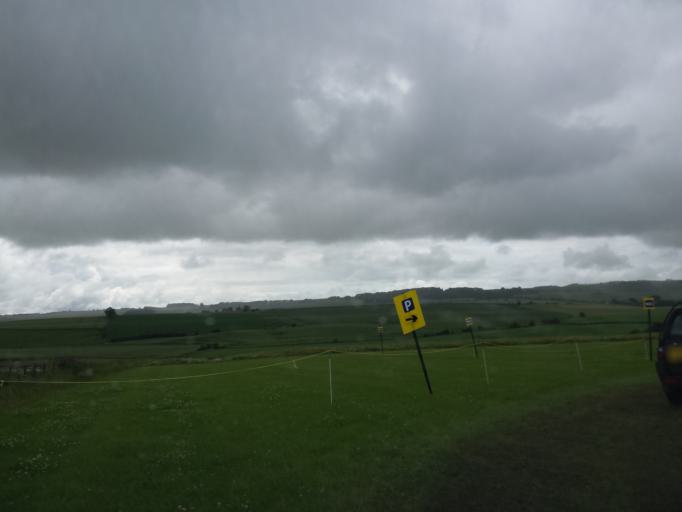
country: GB
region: Scotland
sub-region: Fife
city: Leuchars
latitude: 56.3581
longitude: -2.9028
